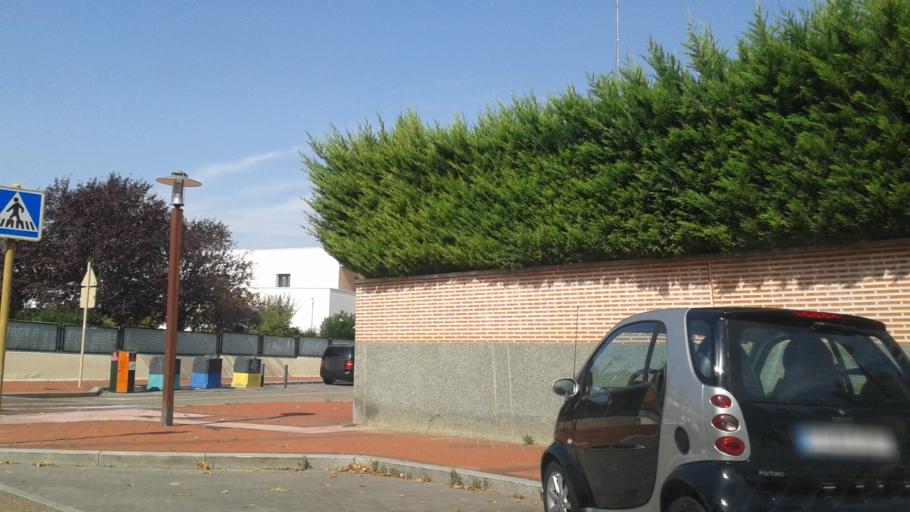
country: ES
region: Castille and Leon
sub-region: Provincia de Valladolid
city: Arroyo
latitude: 41.6110
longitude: -4.7891
